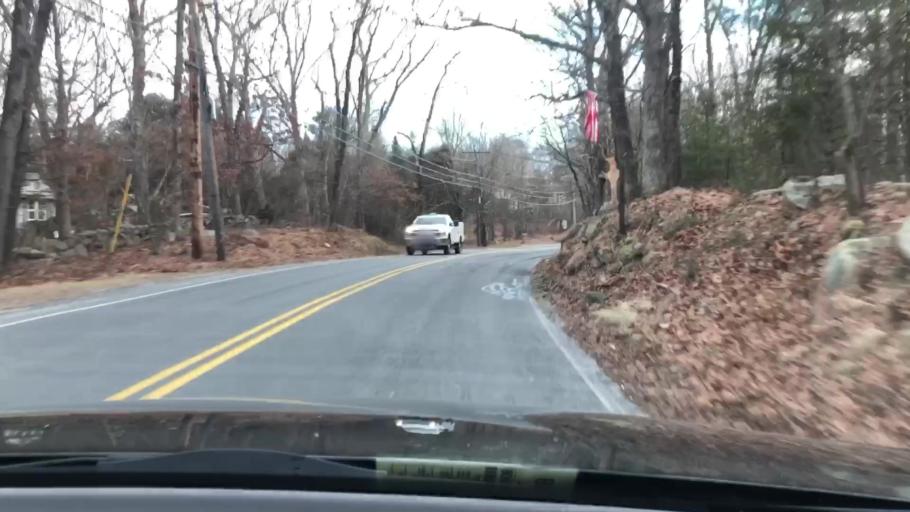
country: US
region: Massachusetts
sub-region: Worcester County
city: Mendon
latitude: 42.0758
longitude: -71.5260
